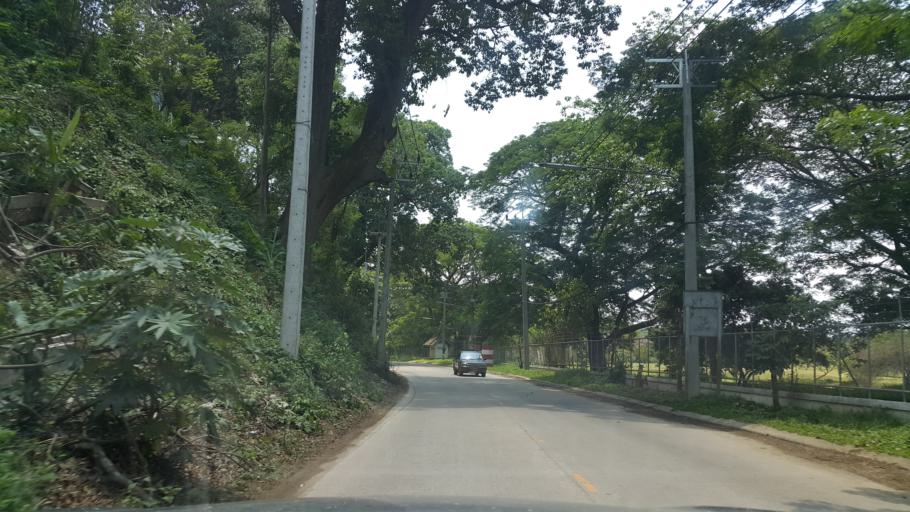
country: TH
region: Chiang Rai
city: Chiang Rai
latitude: 19.9160
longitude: 99.8224
